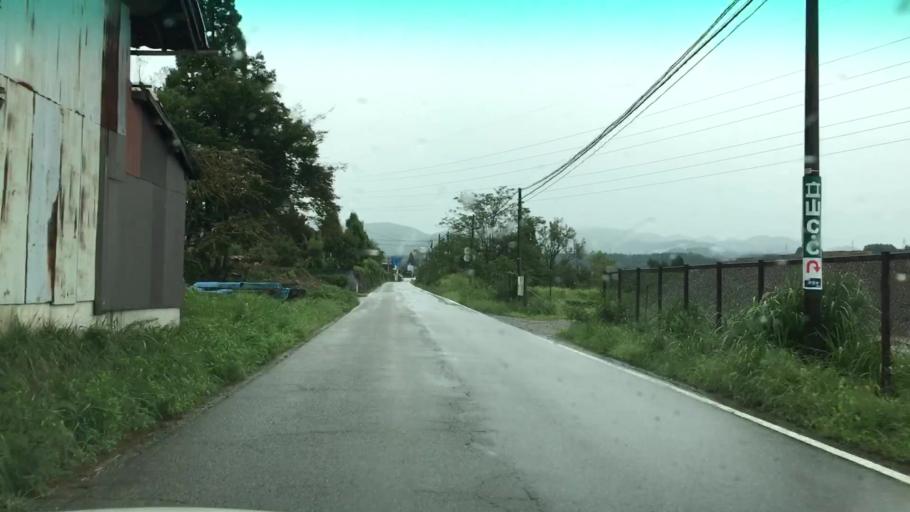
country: JP
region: Toyama
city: Kamiichi
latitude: 36.6148
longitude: 137.3218
